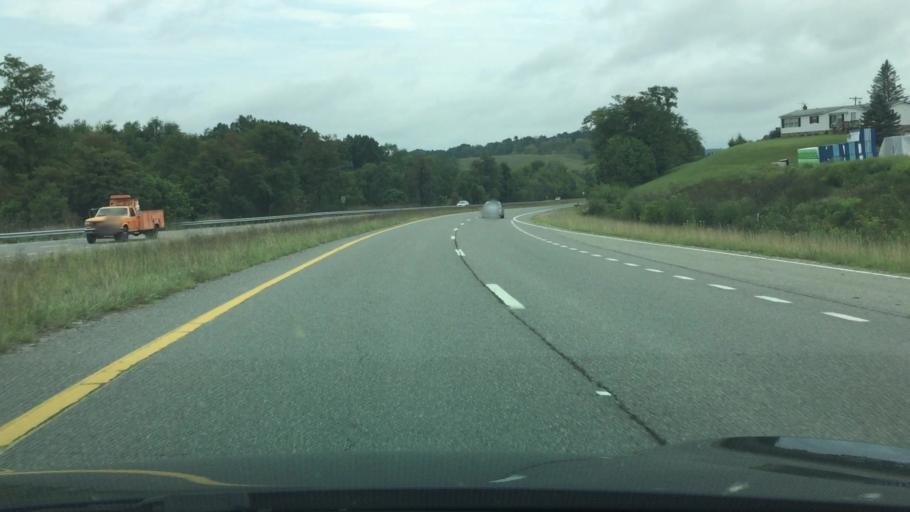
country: US
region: Virginia
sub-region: City of Radford
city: Radford
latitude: 37.1016
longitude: -80.5162
